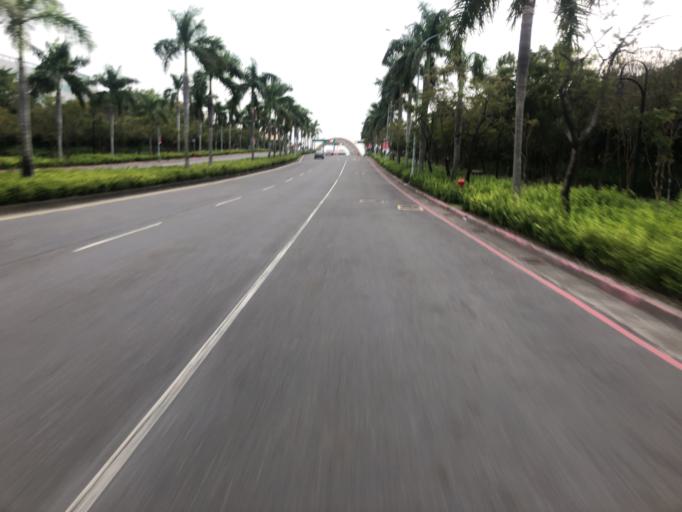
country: TW
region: Taiwan
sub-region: Tainan
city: Tainan
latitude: 23.0932
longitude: 120.2819
